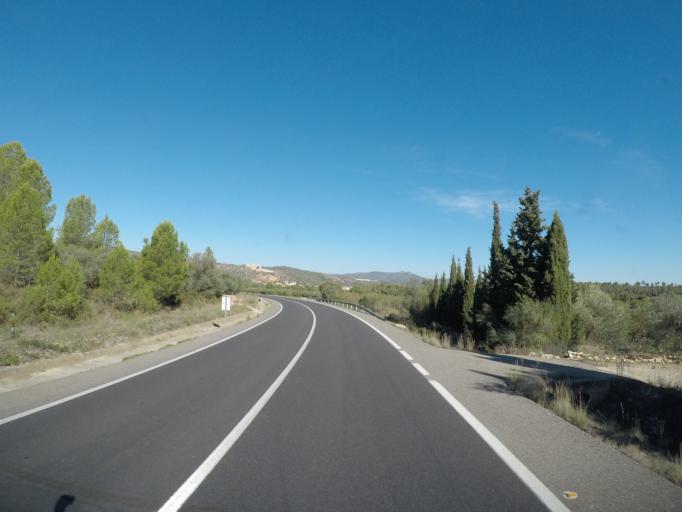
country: ES
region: Catalonia
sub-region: Provincia de Tarragona
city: Rasquera
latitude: 41.0210
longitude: 0.6079
